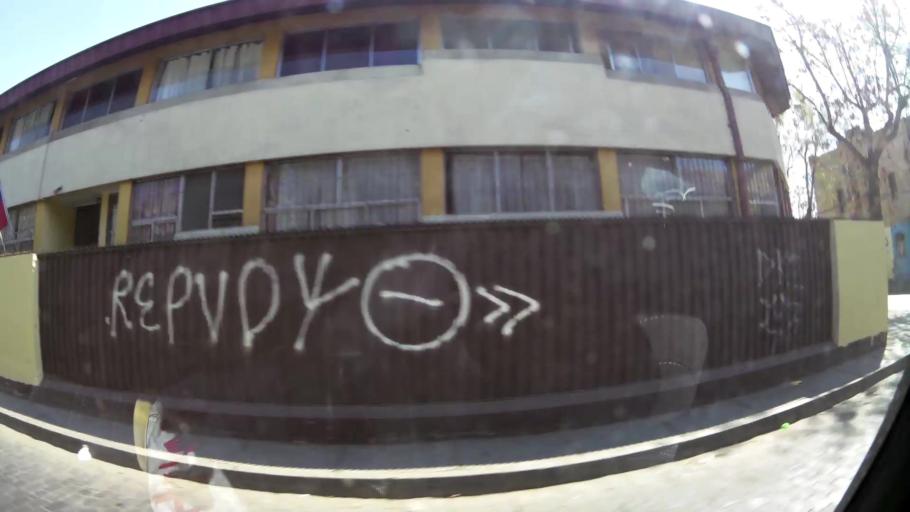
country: CL
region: Santiago Metropolitan
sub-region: Provincia de Santiago
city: Santiago
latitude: -33.4328
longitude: -70.6631
